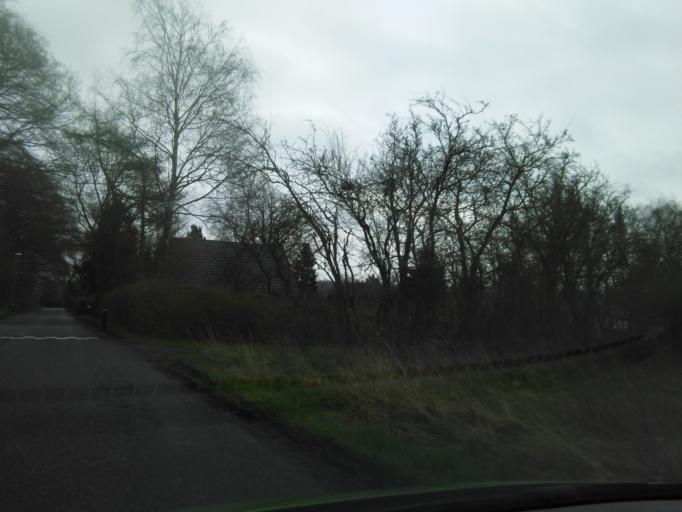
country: DK
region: Central Jutland
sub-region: Arhus Kommune
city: Kolt
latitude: 56.1506
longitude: 10.0797
